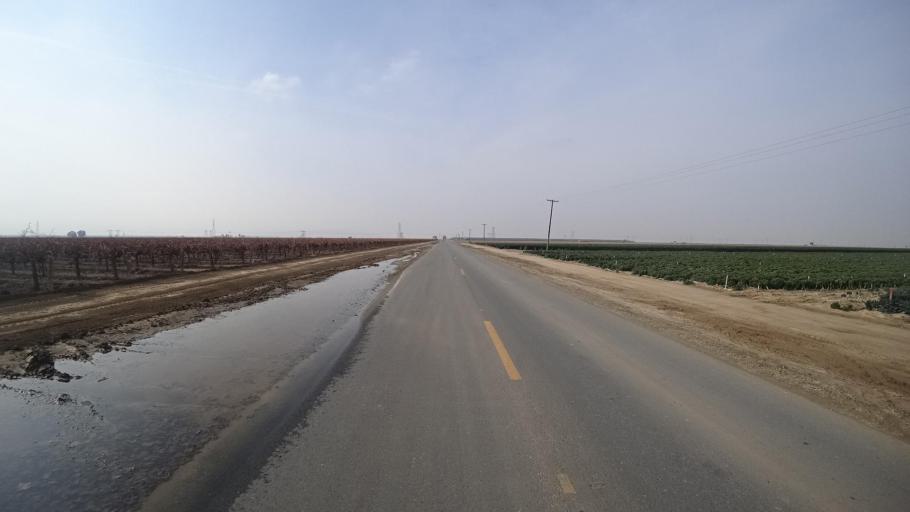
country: US
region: California
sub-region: Kern County
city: Arvin
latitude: 35.0454
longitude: -118.8660
